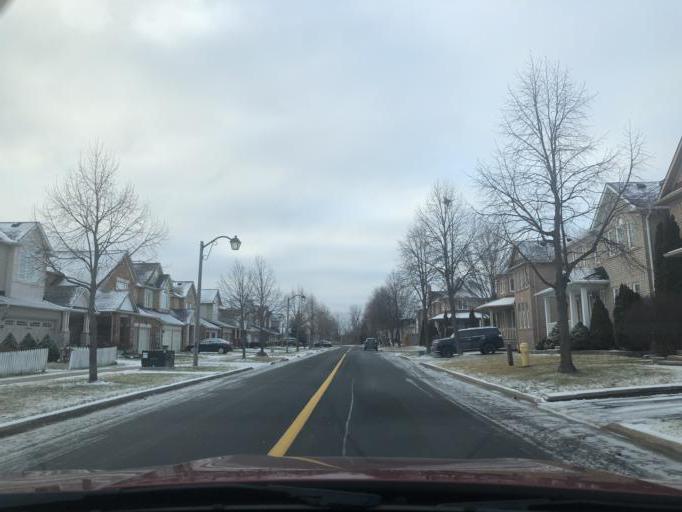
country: CA
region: Ontario
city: Markham
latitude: 43.8658
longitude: -79.2359
